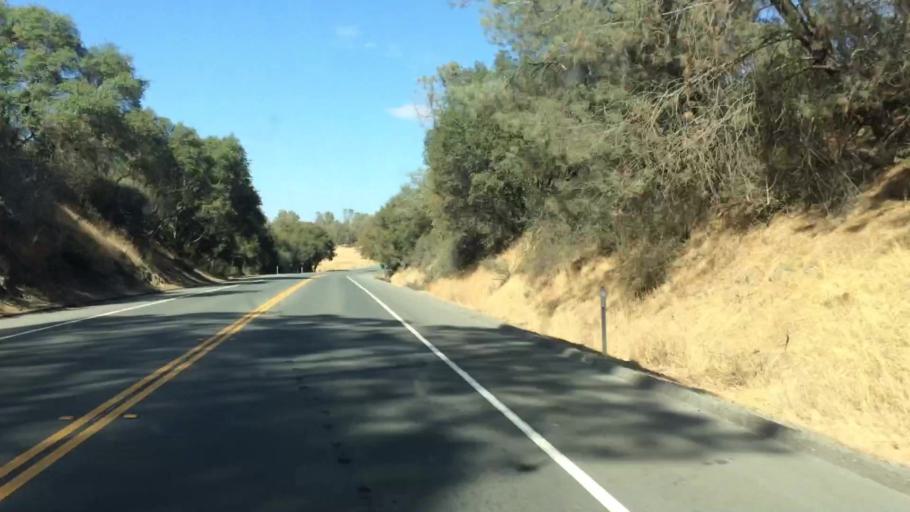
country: US
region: California
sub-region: Amador County
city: Ione
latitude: 38.3869
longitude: -120.9079
